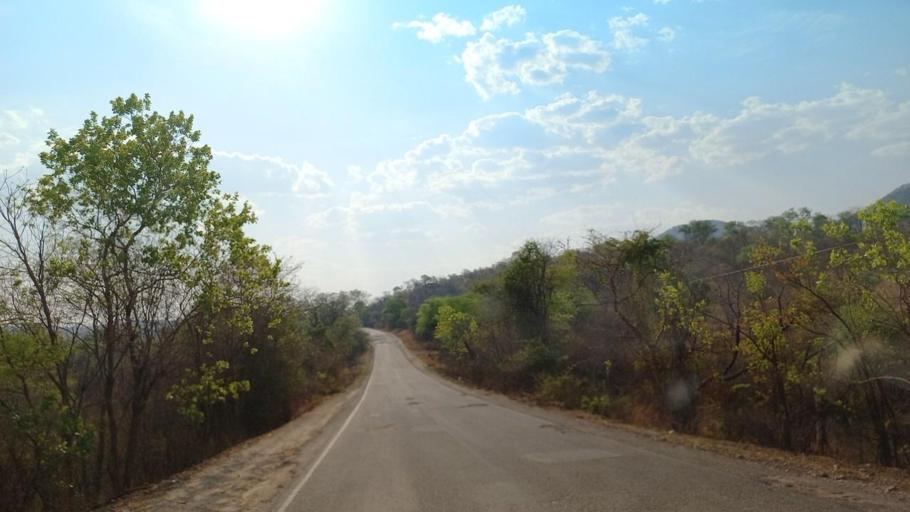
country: ZM
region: Lusaka
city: Luangwa
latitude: -14.9827
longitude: 30.1656
